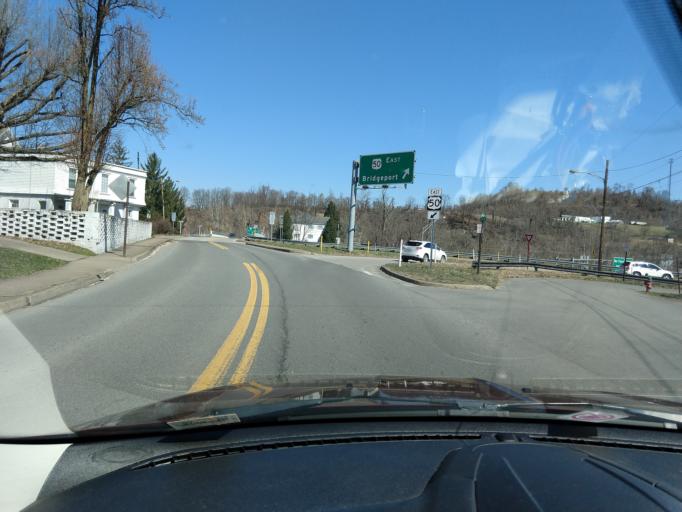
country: US
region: West Virginia
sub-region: Harrison County
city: Clarksburg
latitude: 39.2831
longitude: -80.3438
